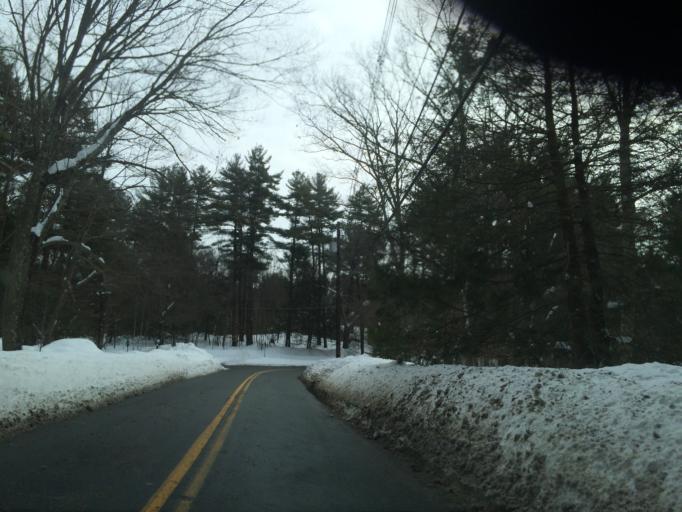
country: US
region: Massachusetts
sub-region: Middlesex County
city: Weston
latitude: 42.3778
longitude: -71.3123
